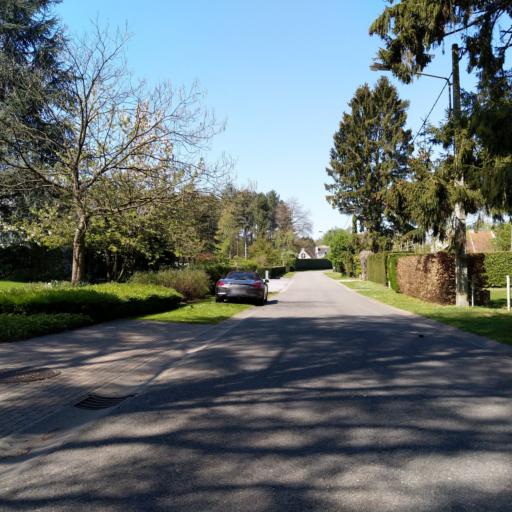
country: BE
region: Wallonia
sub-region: Province du Hainaut
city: Jurbise
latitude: 50.5071
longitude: 3.9261
